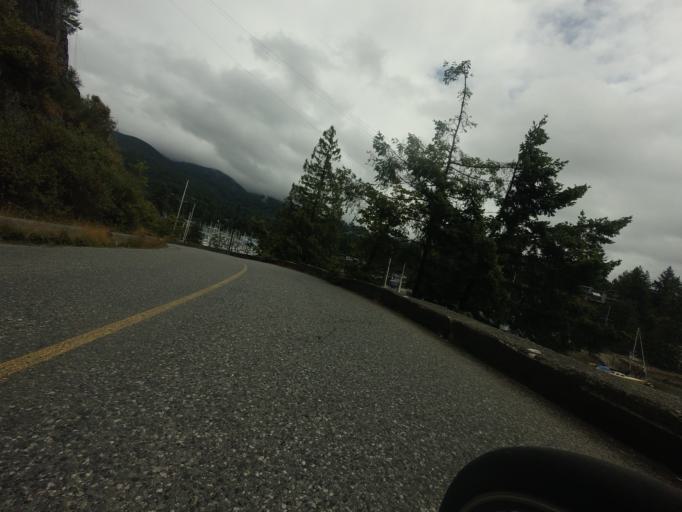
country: CA
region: British Columbia
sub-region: Greater Vancouver Regional District
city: Bowen Island
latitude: 49.3556
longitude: -123.2763
